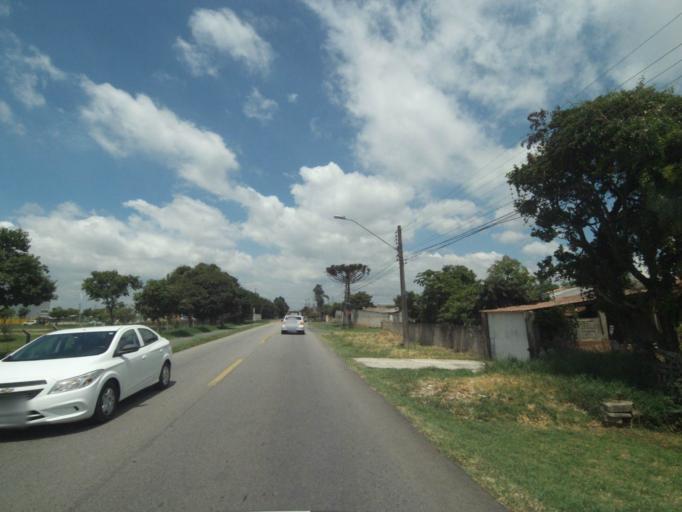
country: BR
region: Parana
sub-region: Pinhais
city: Pinhais
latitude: -25.4780
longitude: -49.1931
